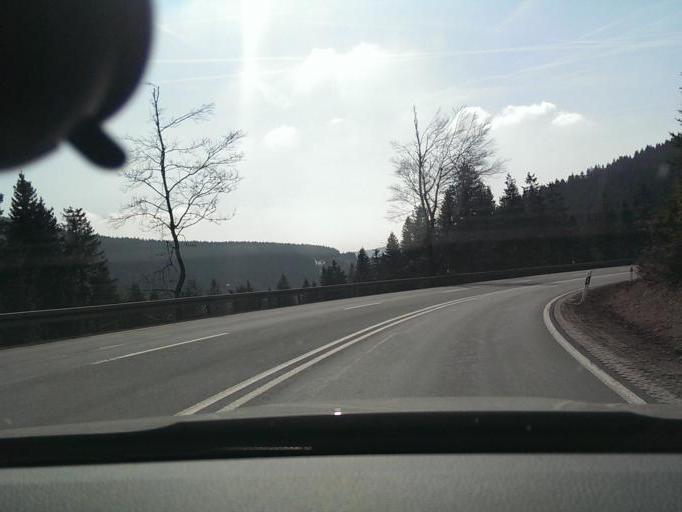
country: DE
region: Thuringia
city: Oberhof
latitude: 50.6864
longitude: 10.7053
